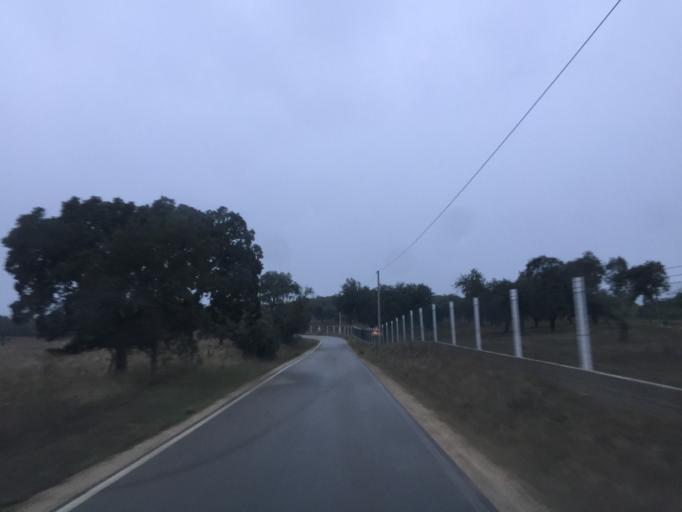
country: PT
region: Portalegre
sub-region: Avis
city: Avis
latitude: 39.0501
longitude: -7.9040
